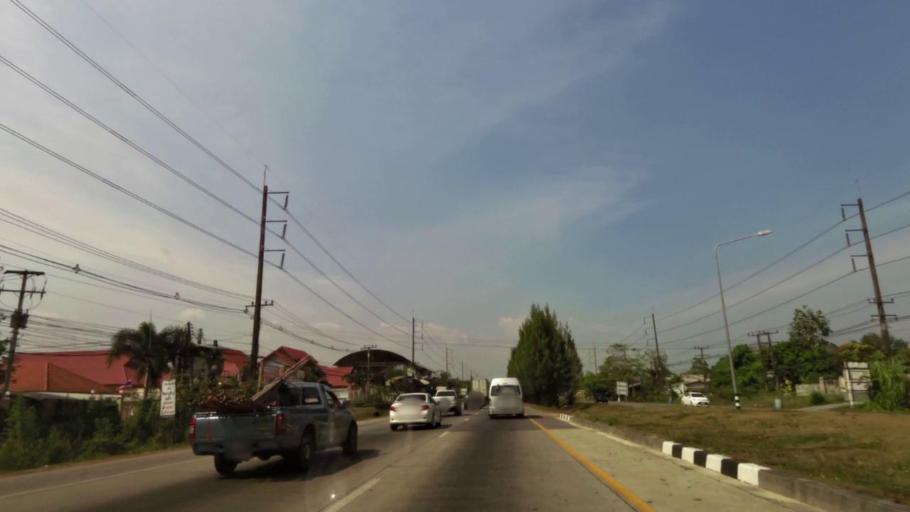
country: TH
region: Chanthaburi
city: Chanthaburi
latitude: 12.6516
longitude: 102.1279
